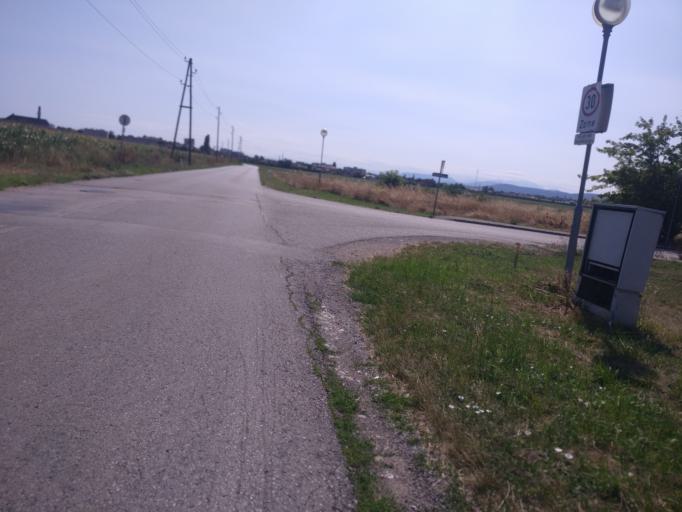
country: AT
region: Lower Austria
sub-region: Politischer Bezirk Modling
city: Guntramsdorf
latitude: 48.0357
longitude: 16.3095
